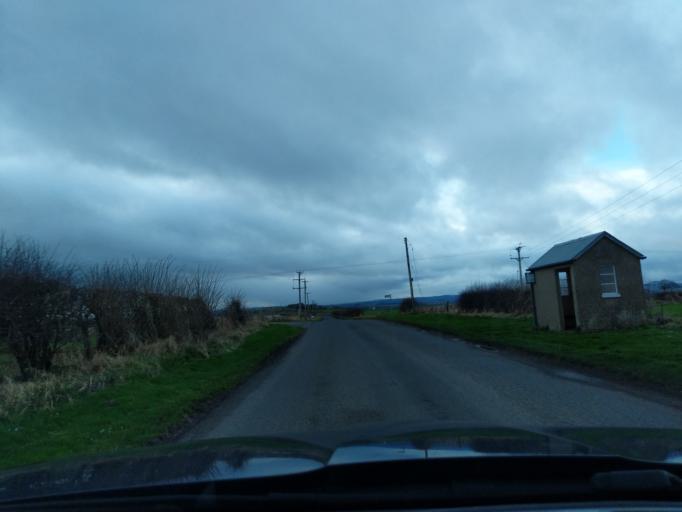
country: GB
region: England
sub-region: Northumberland
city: Ancroft
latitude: 55.7134
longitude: -2.0709
